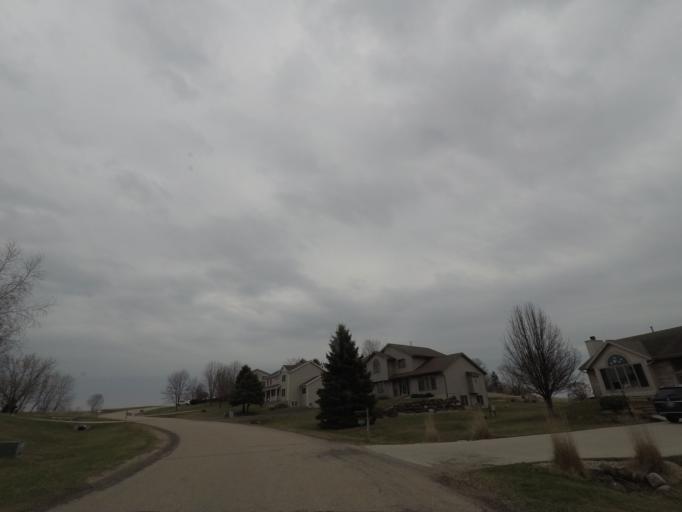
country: US
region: Wisconsin
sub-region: Dane County
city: Middleton
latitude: 43.1173
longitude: -89.5731
